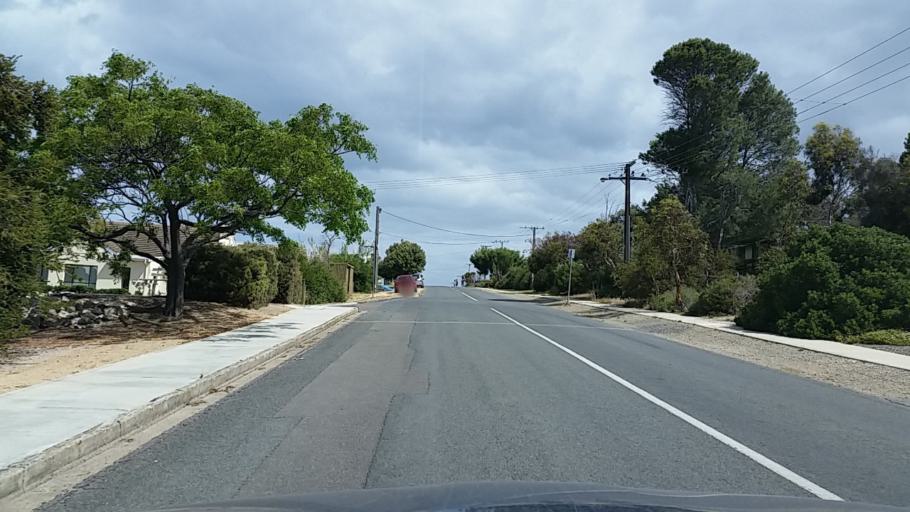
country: AU
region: South Australia
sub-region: Alexandrina
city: Port Elliot
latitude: -35.5328
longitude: 138.6773
